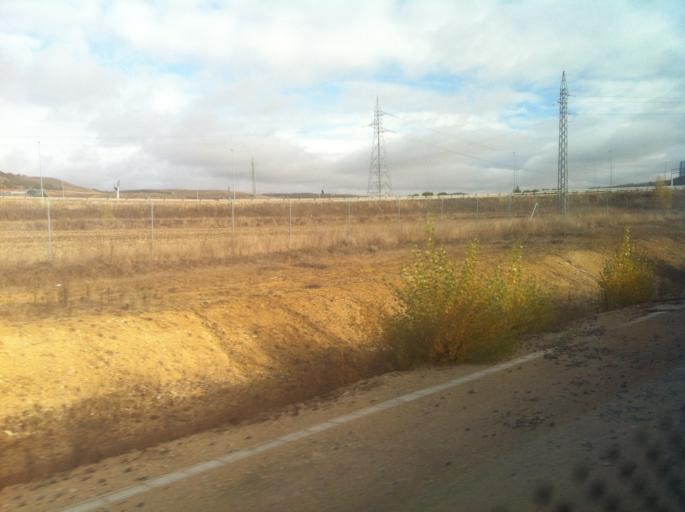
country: ES
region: Castille and Leon
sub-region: Provincia de Burgos
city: Burgos
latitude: 42.3736
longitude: -3.6560
